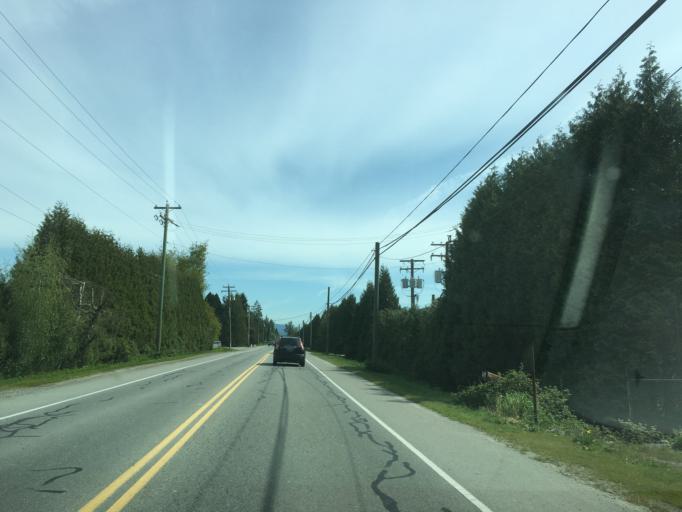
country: CA
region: British Columbia
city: Pitt Meadows
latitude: 49.2443
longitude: -122.7118
